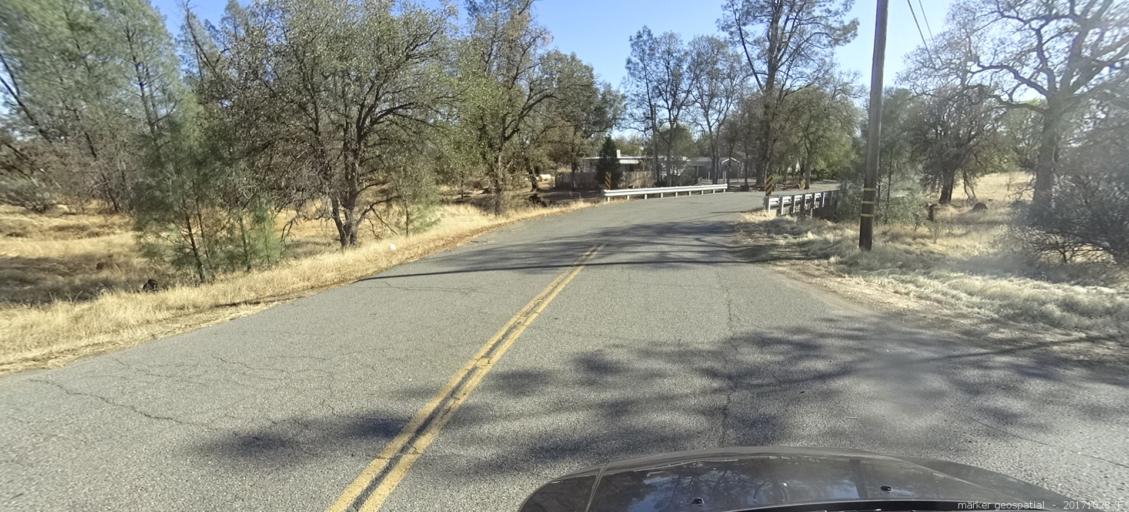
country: US
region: California
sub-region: Shasta County
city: Central Valley (historical)
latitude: 40.6402
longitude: -122.3752
